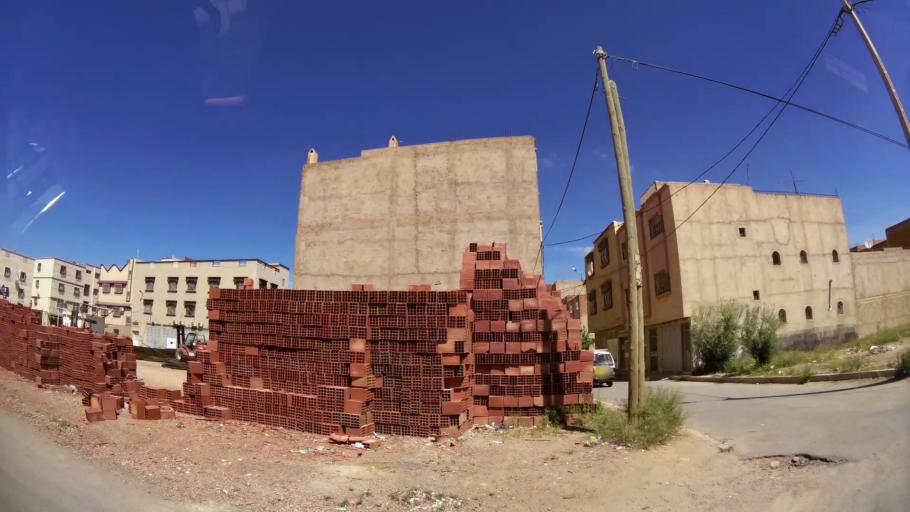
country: MA
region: Oriental
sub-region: Oujda-Angad
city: Oujda
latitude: 34.6698
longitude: -1.9326
